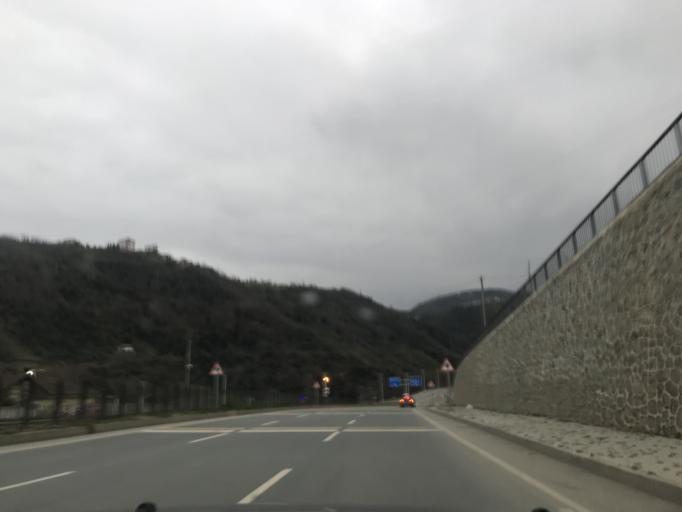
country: TR
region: Trabzon
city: Akcaabat
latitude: 41.0018
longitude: 39.6269
